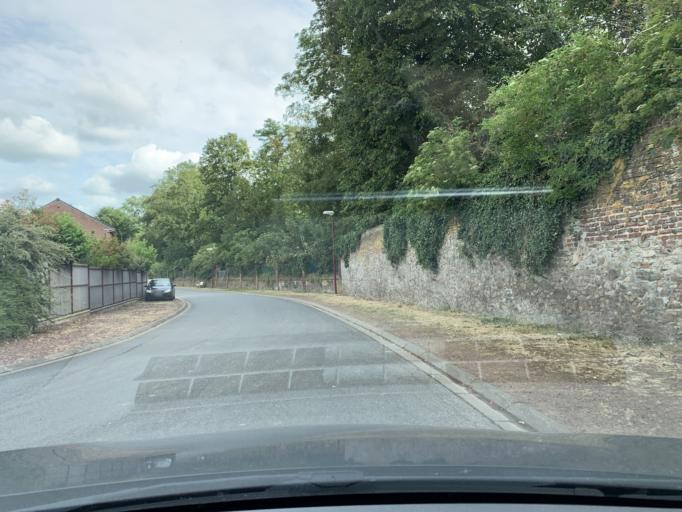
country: FR
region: Nord-Pas-de-Calais
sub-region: Departement du Nord
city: Guesnain
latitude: 50.3279
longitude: 3.1457
